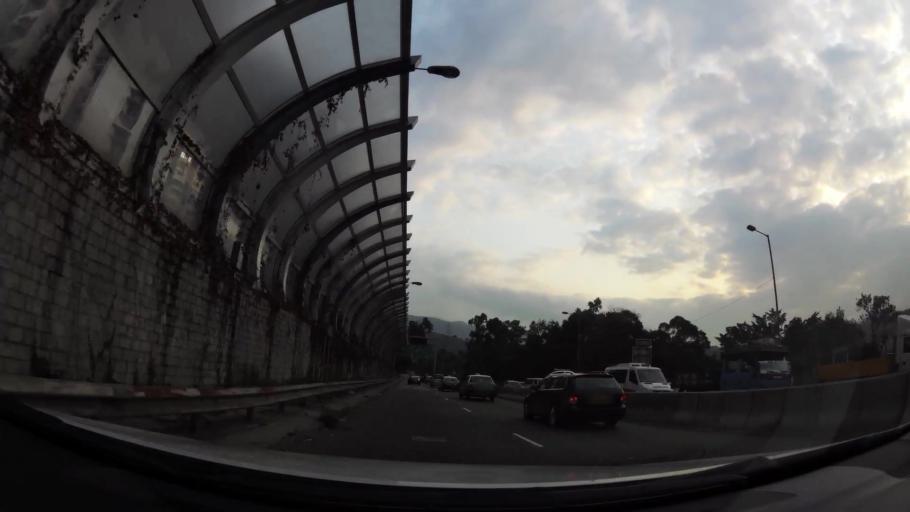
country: HK
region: Tai Po
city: Tai Po
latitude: 22.4518
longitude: 114.1588
